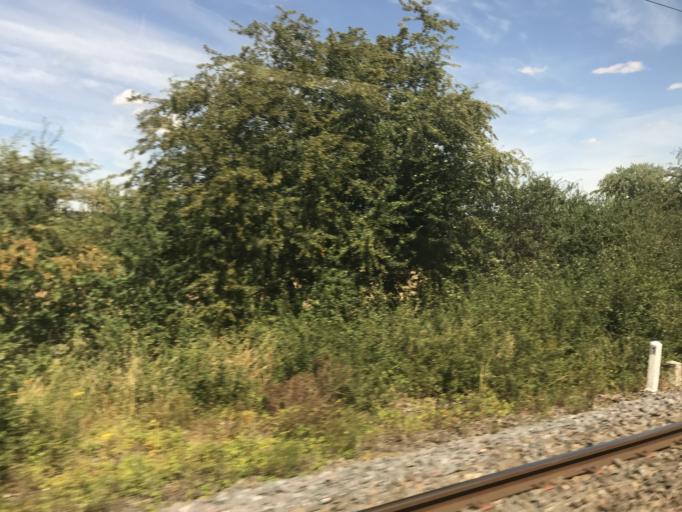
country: FR
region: Lorraine
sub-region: Departement de la Moselle
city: Crehange
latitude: 48.9645
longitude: 6.5601
